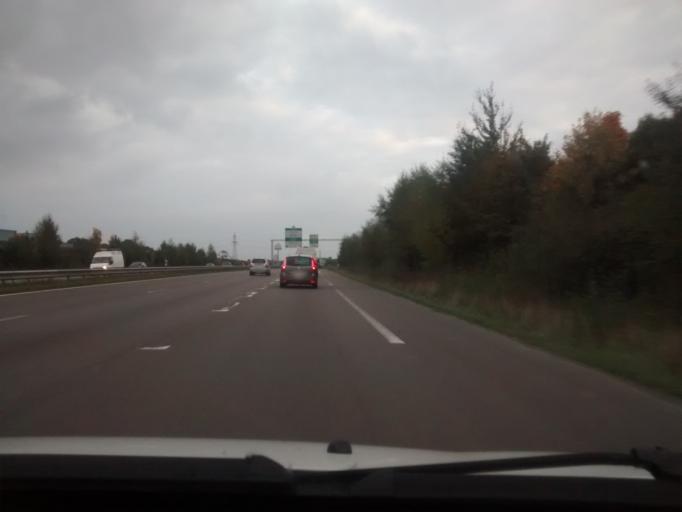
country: FR
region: Brittany
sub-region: Departement d'Ille-et-Vilaine
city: Saint-Gregoire
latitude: 48.1486
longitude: -1.6993
